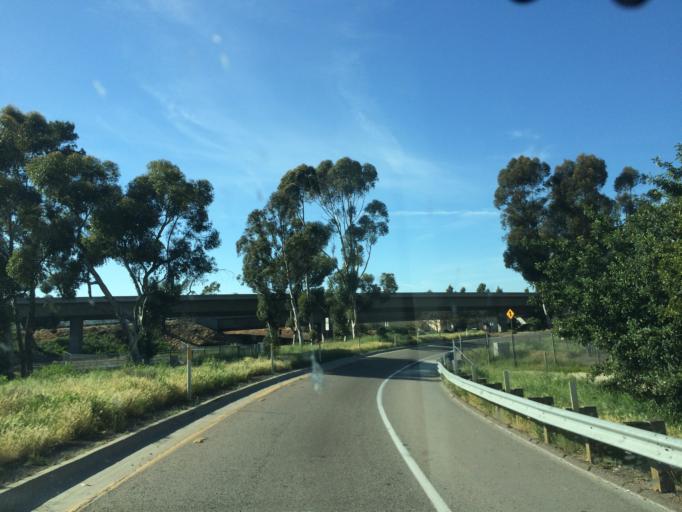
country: US
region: California
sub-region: San Diego County
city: El Cajon
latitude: 32.8033
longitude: -116.9600
